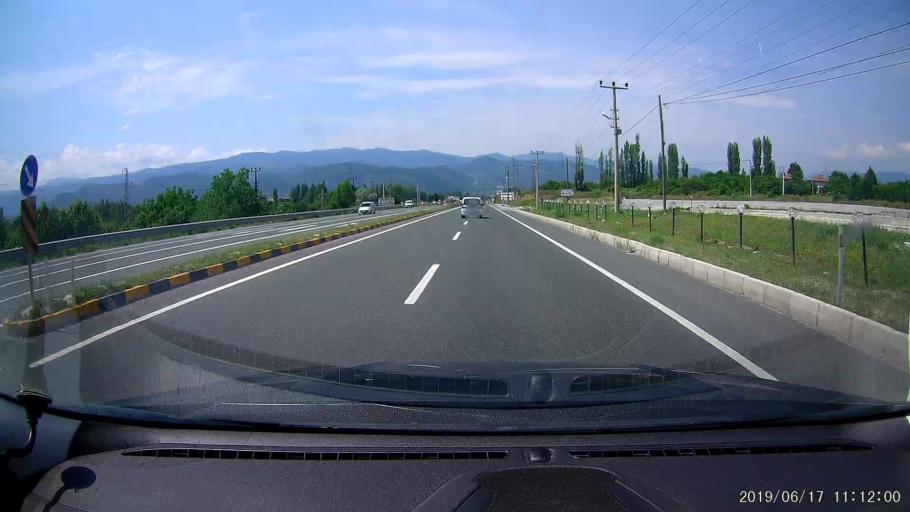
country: TR
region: Kastamonu
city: Tosya
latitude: 40.9788
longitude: 34.0020
